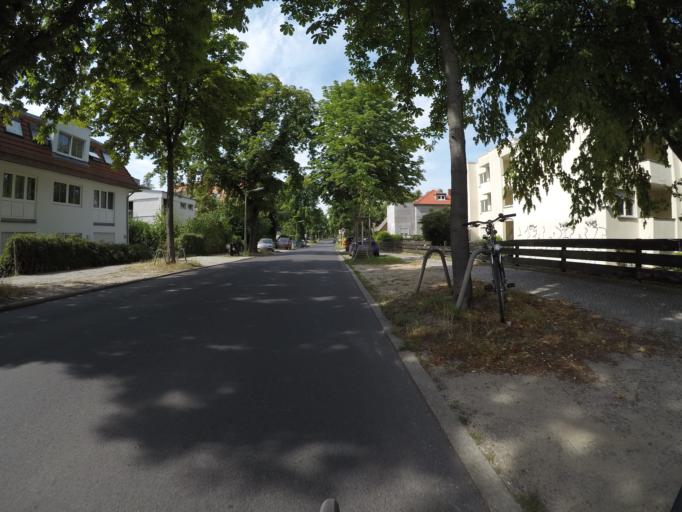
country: DE
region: Berlin
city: Lankwitz
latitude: 52.4212
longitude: 13.3499
